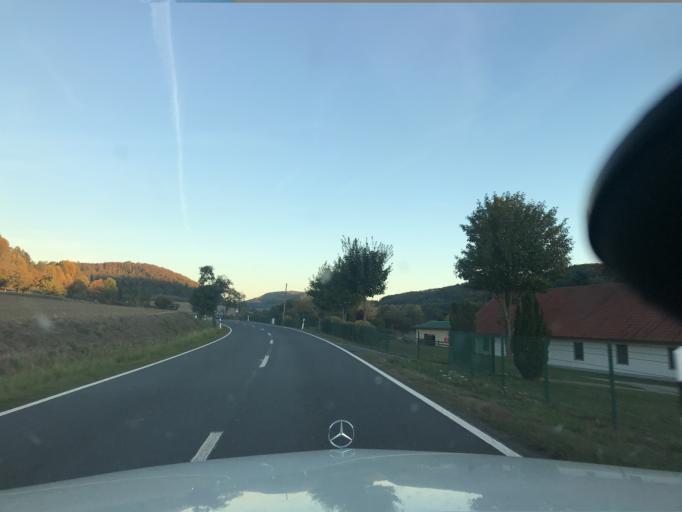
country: DE
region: Thuringia
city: Geismar
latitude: 51.2283
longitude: 10.1750
